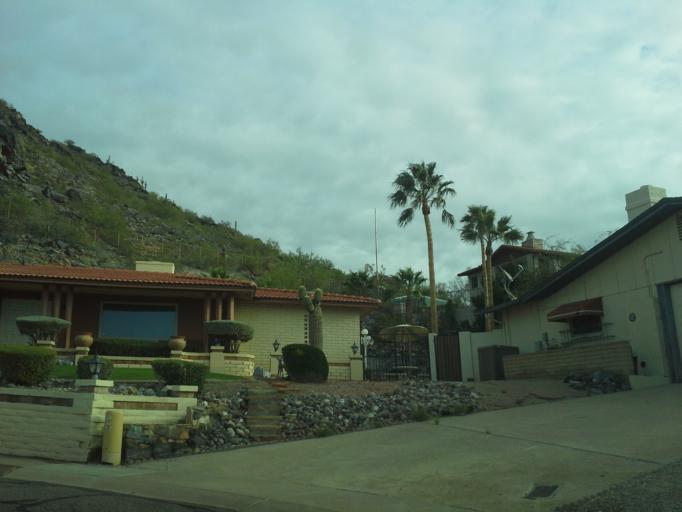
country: US
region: Arizona
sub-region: Maricopa County
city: Paradise Valley
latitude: 33.5379
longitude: -112.0296
